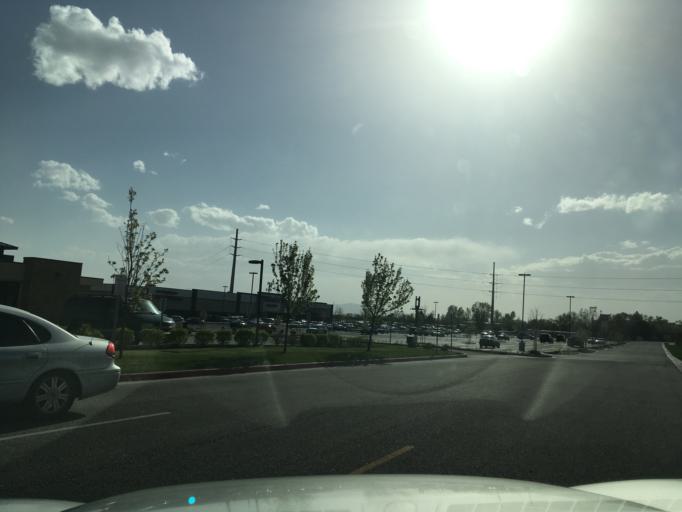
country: US
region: Utah
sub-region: Davis County
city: Layton
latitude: 41.0590
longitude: -111.9578
